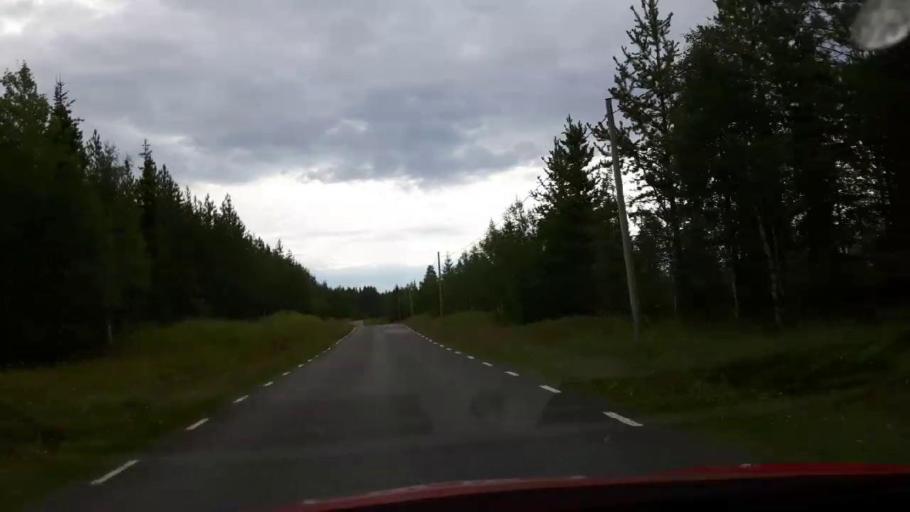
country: SE
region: Jaemtland
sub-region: OEstersunds Kommun
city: Lit
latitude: 63.3780
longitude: 15.0776
